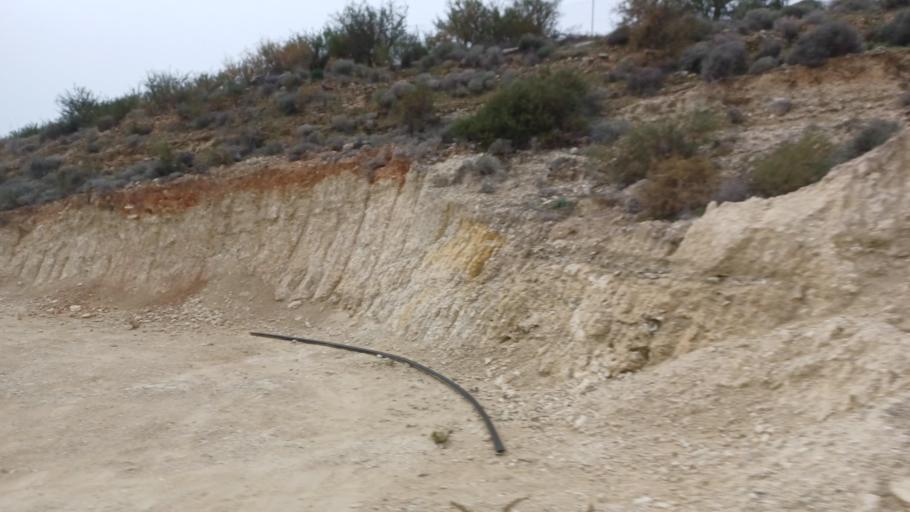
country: CY
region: Limassol
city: Pissouri
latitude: 34.7164
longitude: 32.7417
